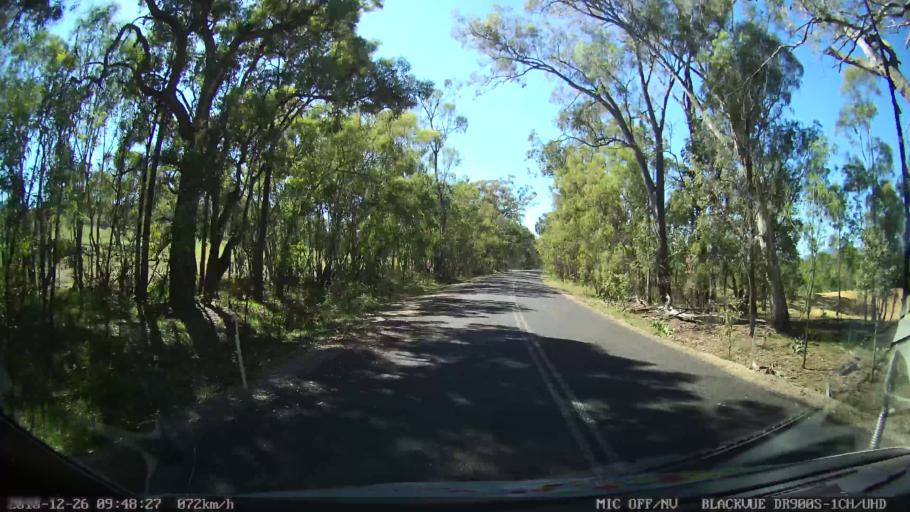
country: AU
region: New South Wales
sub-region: Mid-Western Regional
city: Kandos
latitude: -32.9868
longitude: 150.1150
